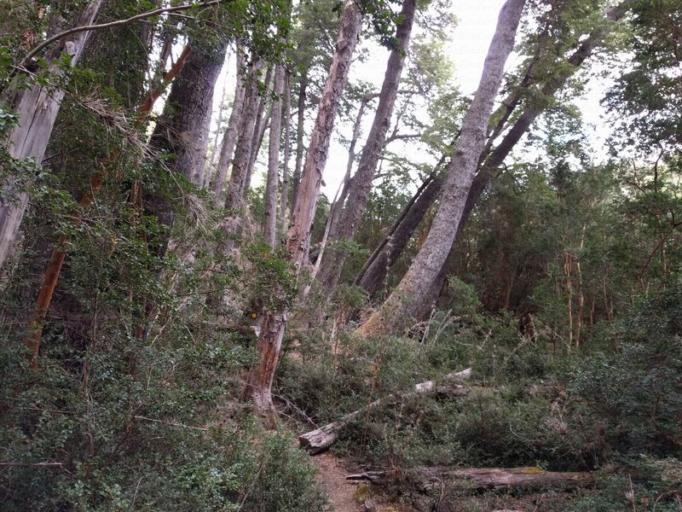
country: AR
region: Chubut
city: Trevelin
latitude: -42.7443
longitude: -71.7425
